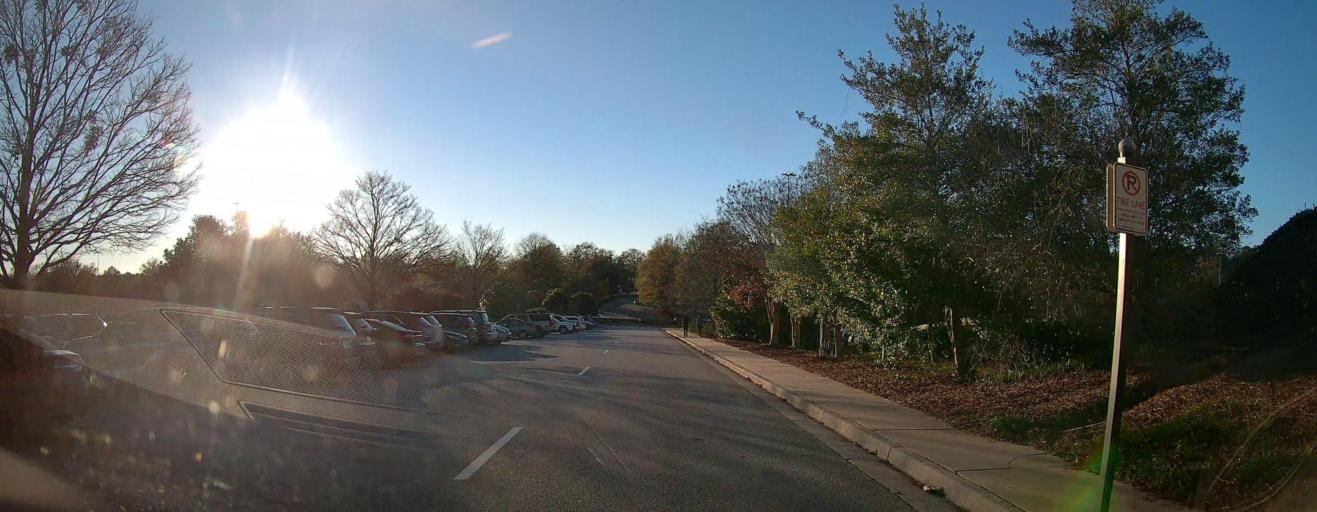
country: US
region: Georgia
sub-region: Gwinnett County
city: Buford
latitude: 34.0633
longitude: -83.9866
